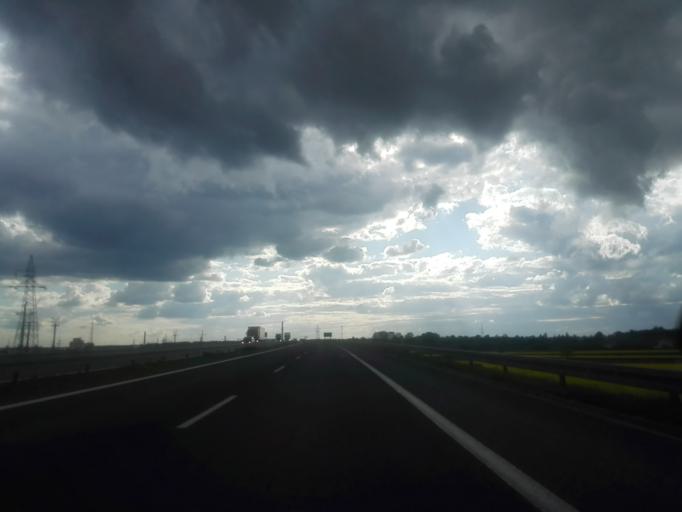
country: PL
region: Masovian Voivodeship
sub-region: Powiat ostrowski
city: Ostrow Mazowiecka
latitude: 52.8207
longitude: 21.9046
